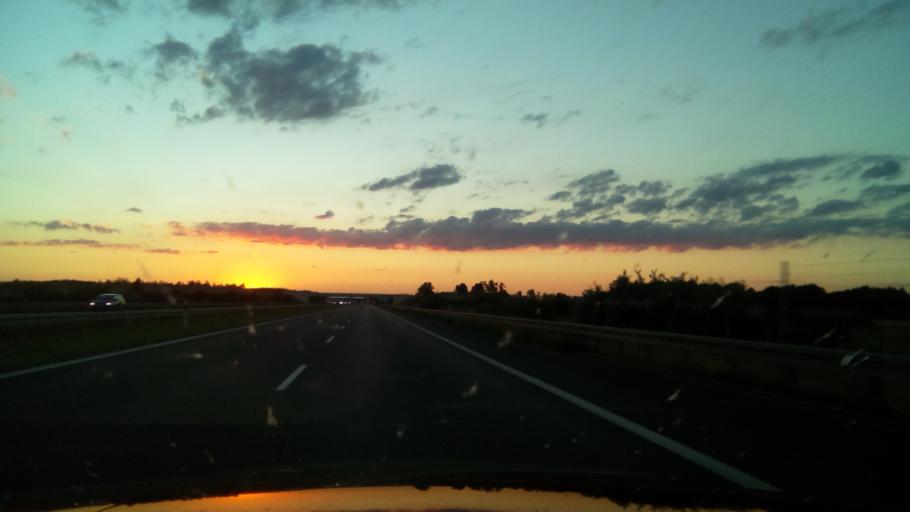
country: PL
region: Greater Poland Voivodeship
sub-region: Powiat kolski
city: Dabie
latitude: 52.0552
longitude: 18.8416
